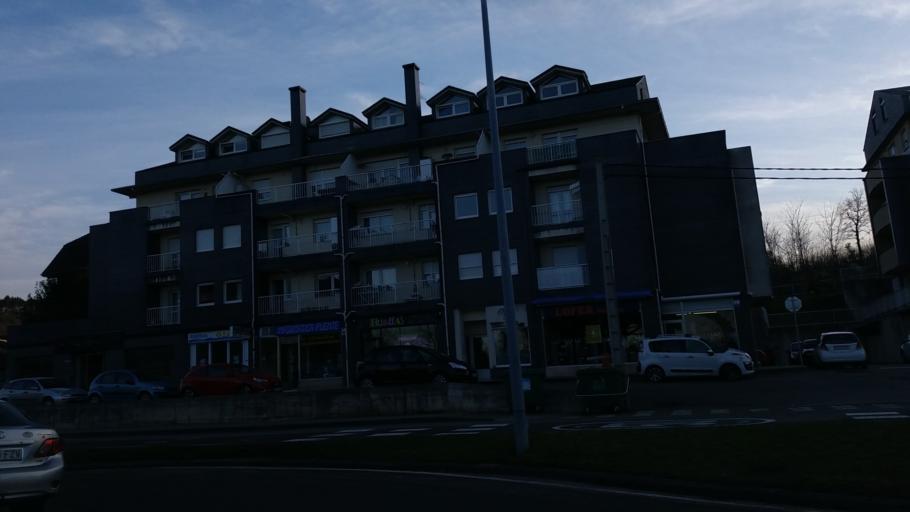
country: ES
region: Cantabria
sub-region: Provincia de Cantabria
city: Reocin
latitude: 43.3585
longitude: -4.0891
